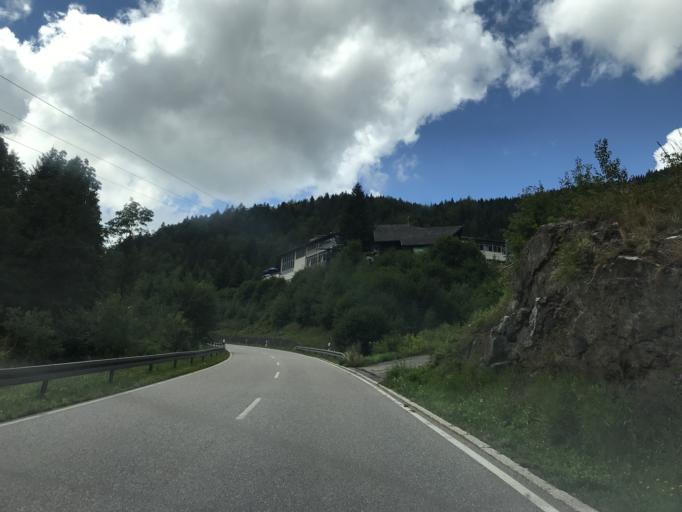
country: DE
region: Baden-Wuerttemberg
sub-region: Freiburg Region
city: Oberried
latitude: 47.9006
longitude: 7.9240
